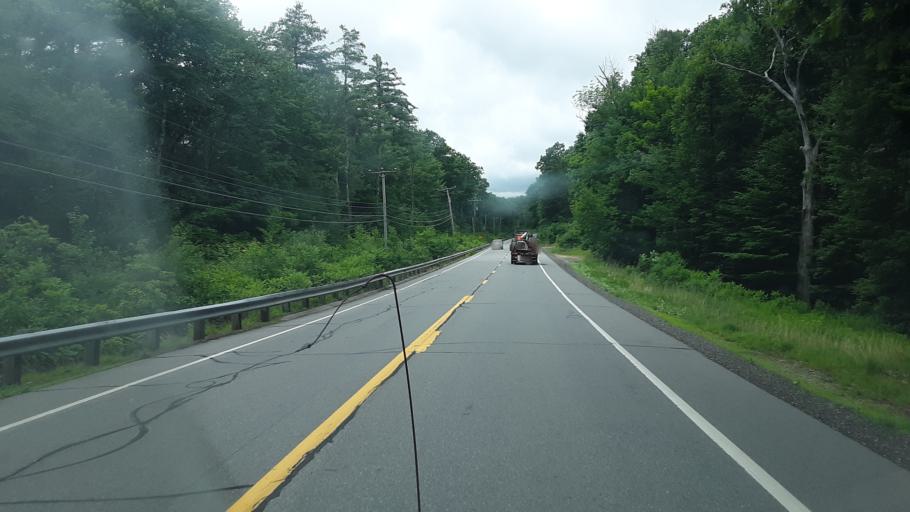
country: US
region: New Hampshire
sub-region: Rockingham County
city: Northwood
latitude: 43.1820
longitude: -71.1186
